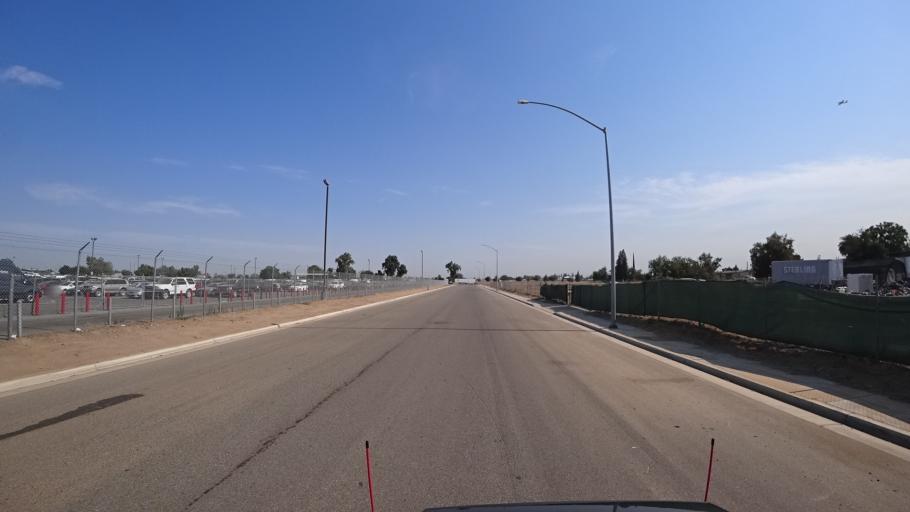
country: US
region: California
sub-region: Fresno County
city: West Park
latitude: 36.7395
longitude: -119.8399
